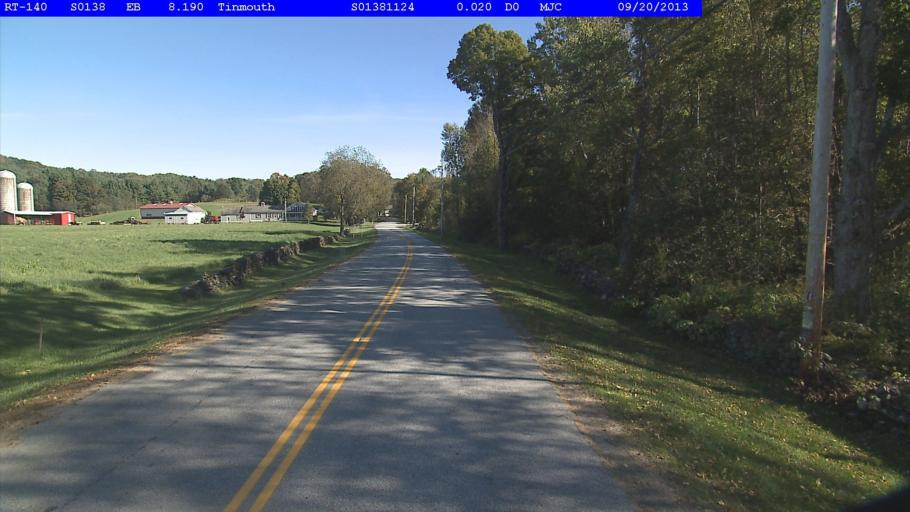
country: US
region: Vermont
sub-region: Rutland County
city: West Rutland
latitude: 43.4827
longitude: -73.0771
